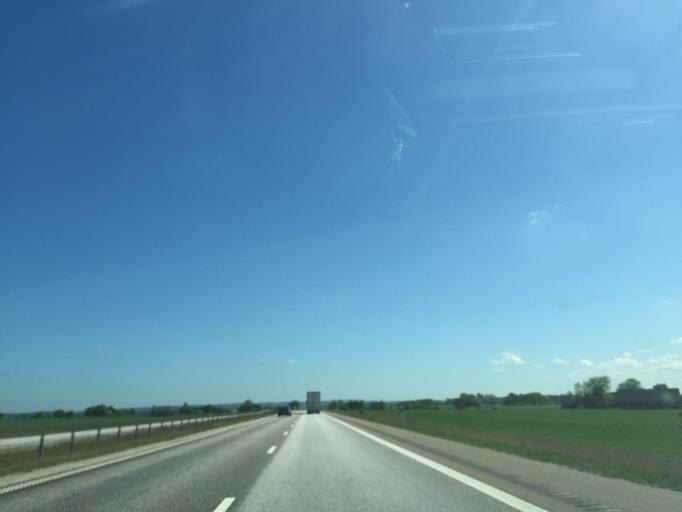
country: SE
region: Skane
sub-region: Astorps Kommun
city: Astorp
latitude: 56.1664
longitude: 12.9775
